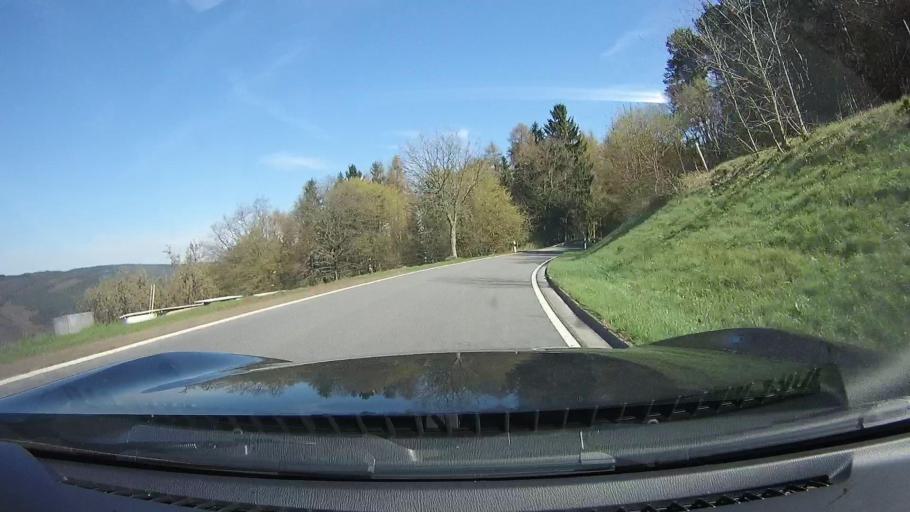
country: DE
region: Hesse
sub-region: Regierungsbezirk Darmstadt
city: Rothenberg
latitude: 49.5064
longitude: 8.9178
